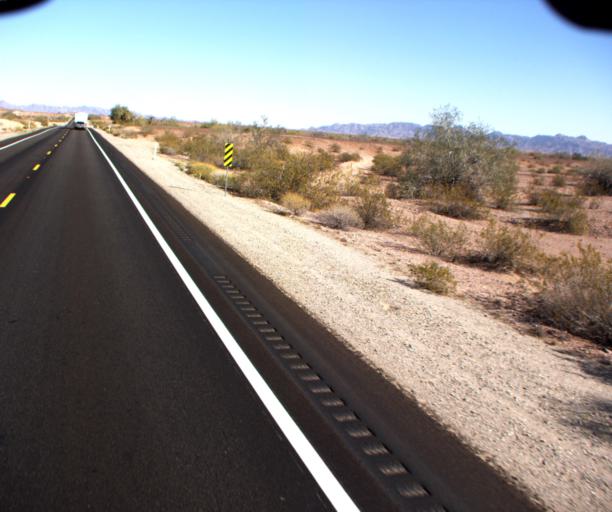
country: US
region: Arizona
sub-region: Yuma County
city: Wellton
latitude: 33.0456
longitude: -114.2905
